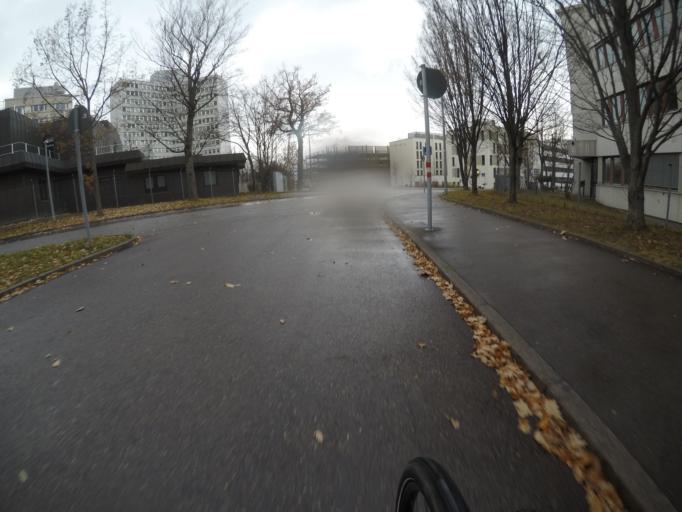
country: DE
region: Baden-Wuerttemberg
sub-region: Regierungsbezirk Stuttgart
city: Stuttgart Feuerbach
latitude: 48.8313
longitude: 9.1540
